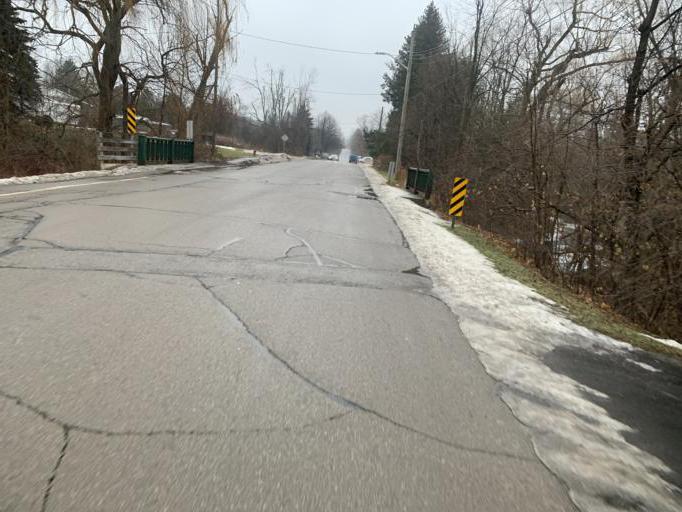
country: CA
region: Ontario
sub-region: Halton
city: Milton
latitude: 43.6579
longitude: -79.9325
